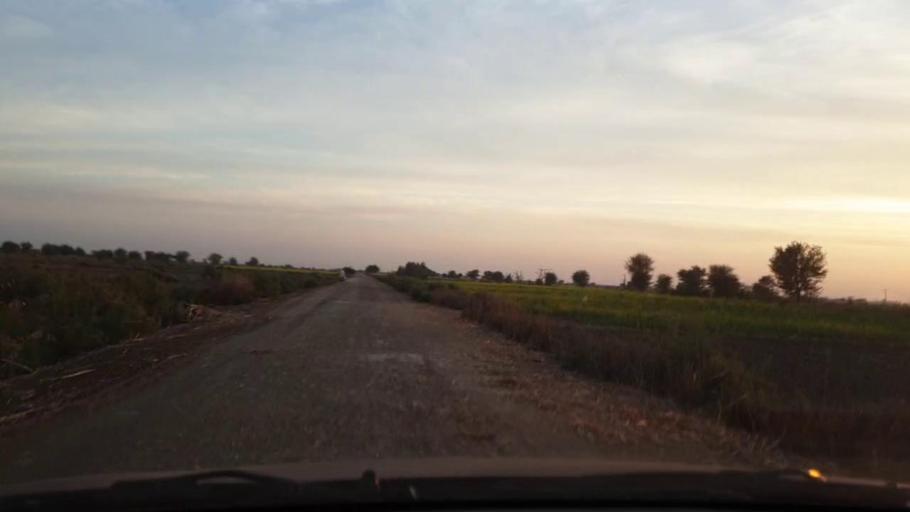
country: PK
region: Sindh
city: Sinjhoro
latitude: 26.0974
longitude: 68.7970
